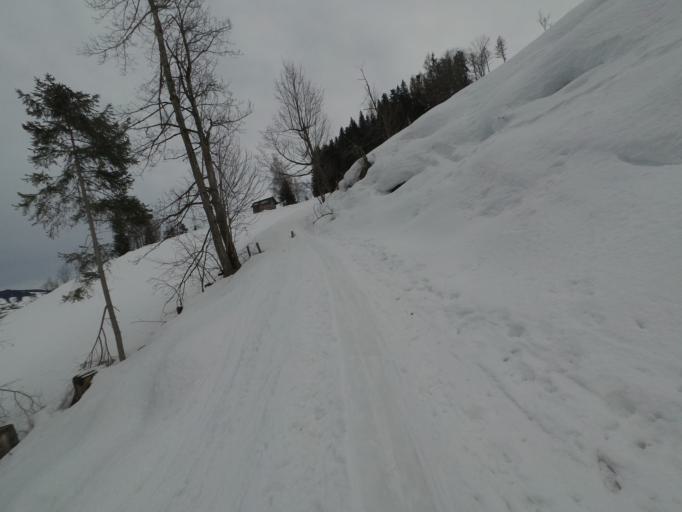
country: AT
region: Salzburg
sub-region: Politischer Bezirk Sankt Johann im Pongau
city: Sankt Johann im Pongau
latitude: 47.3278
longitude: 13.2110
